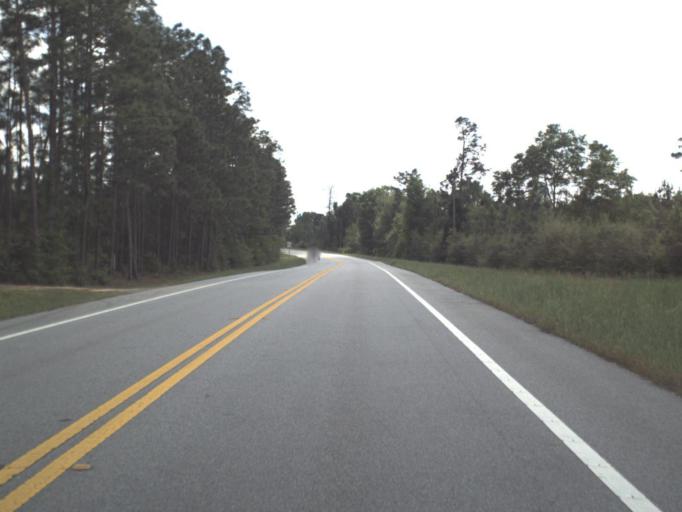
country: US
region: Florida
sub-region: Escambia County
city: Molino
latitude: 30.8017
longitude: -87.4237
